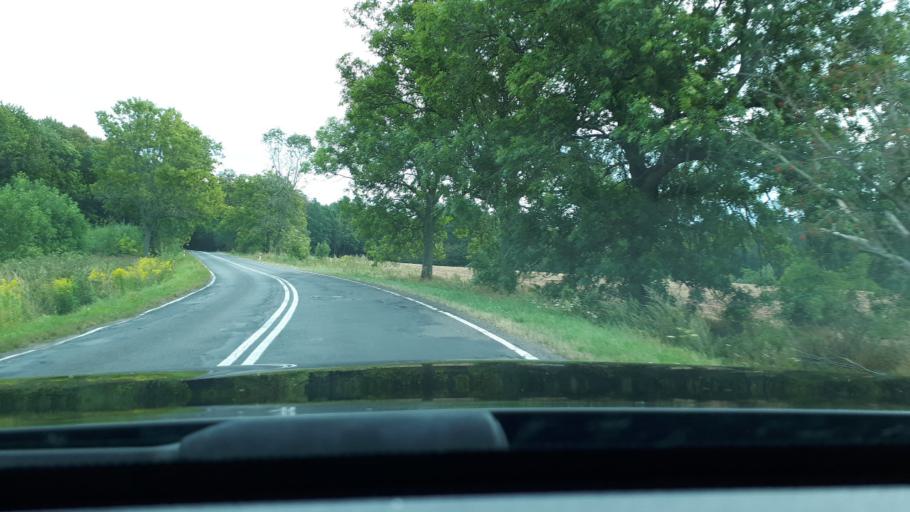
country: PL
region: Lower Silesian Voivodeship
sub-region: Powiat lwowecki
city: Lwowek Slaski
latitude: 51.0983
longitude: 15.5104
